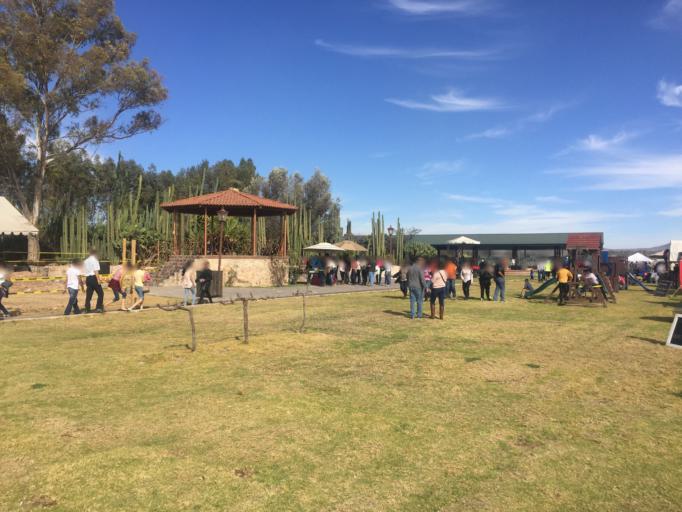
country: MX
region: Queretaro
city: Ezequiel Montes
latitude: 20.6377
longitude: -99.9007
